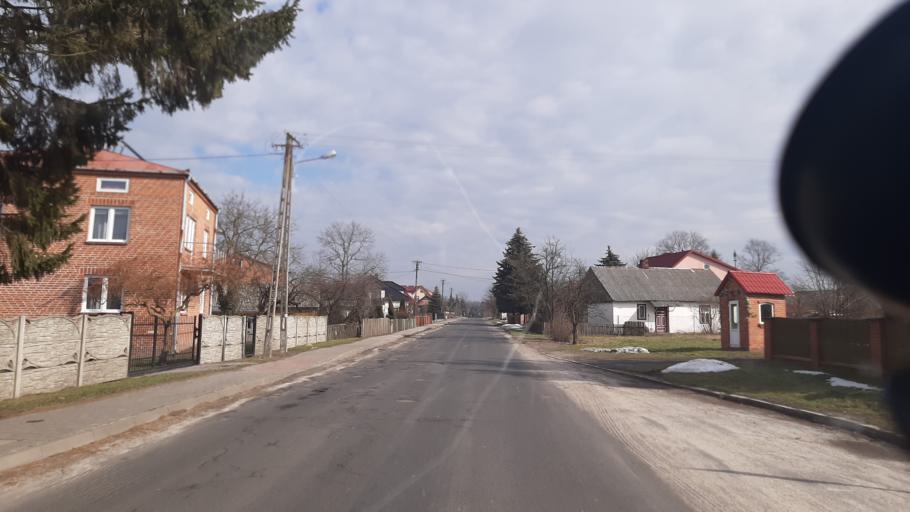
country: PL
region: Lublin Voivodeship
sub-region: Powiat lubartowski
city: Wola Sernicka
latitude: 51.4669
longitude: 22.7318
